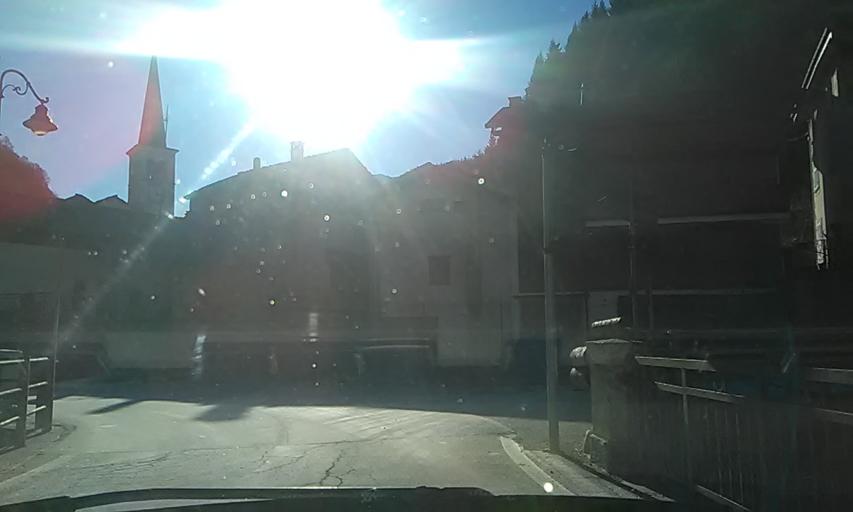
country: IT
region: Piedmont
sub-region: Provincia di Vercelli
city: Rimasco
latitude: 45.8594
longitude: 8.0624
